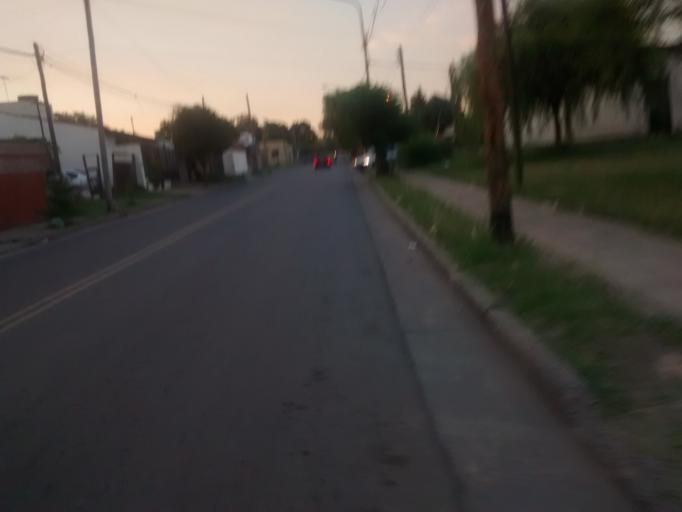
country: AR
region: Buenos Aires
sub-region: Partido de La Plata
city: La Plata
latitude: -34.9423
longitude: -57.9254
